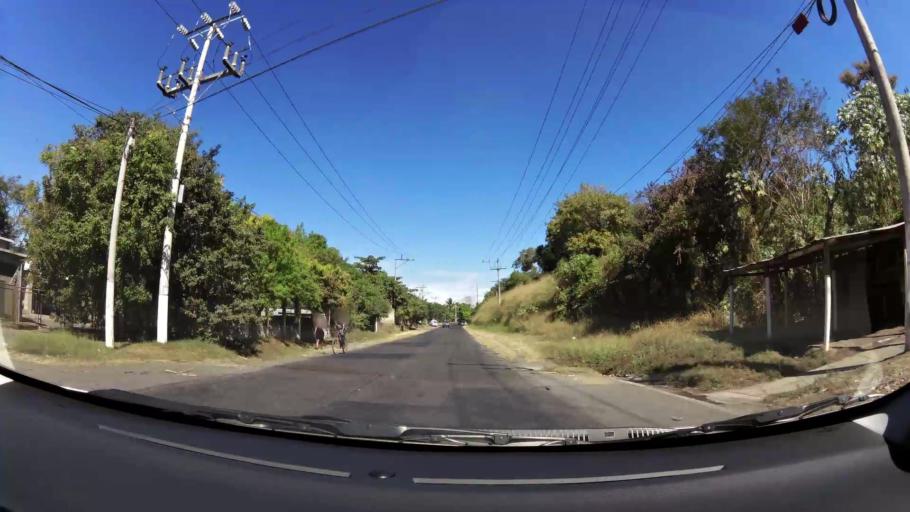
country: SV
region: La Libertad
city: San Juan Opico
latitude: 13.8142
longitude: -89.3562
